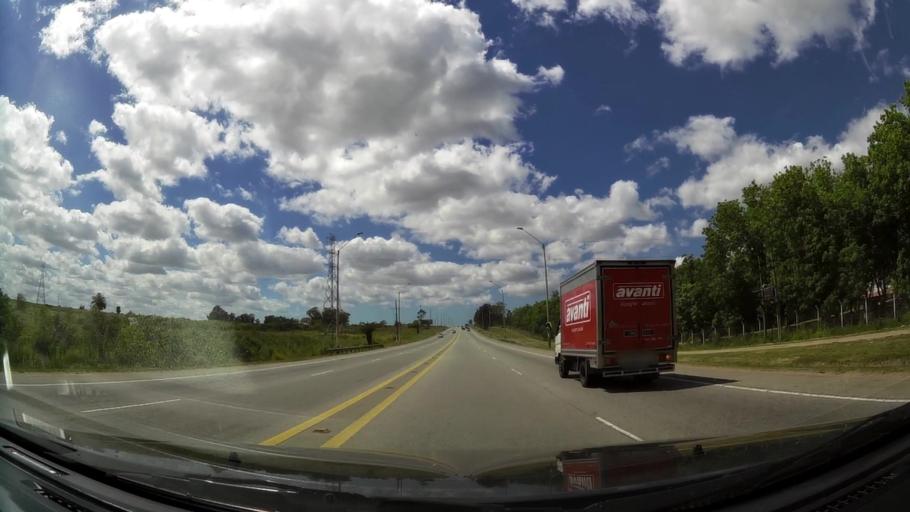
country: UY
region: Canelones
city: Colonia Nicolich
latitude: -34.7978
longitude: -56.0628
